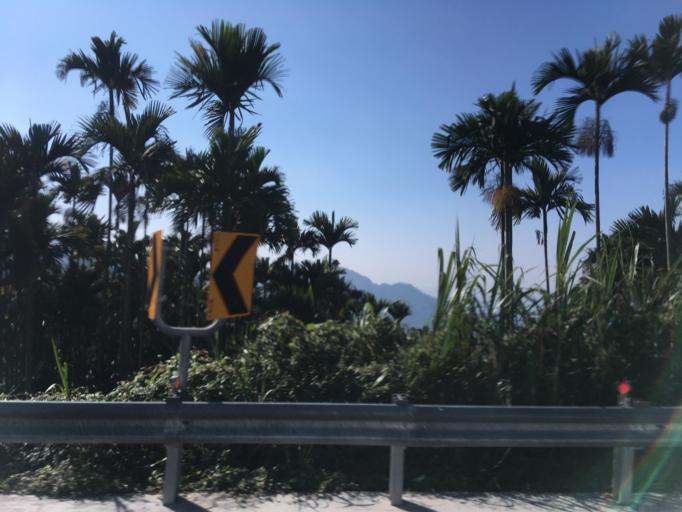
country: TW
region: Taiwan
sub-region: Chiayi
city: Jiayi Shi
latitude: 23.4286
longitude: 120.6413
